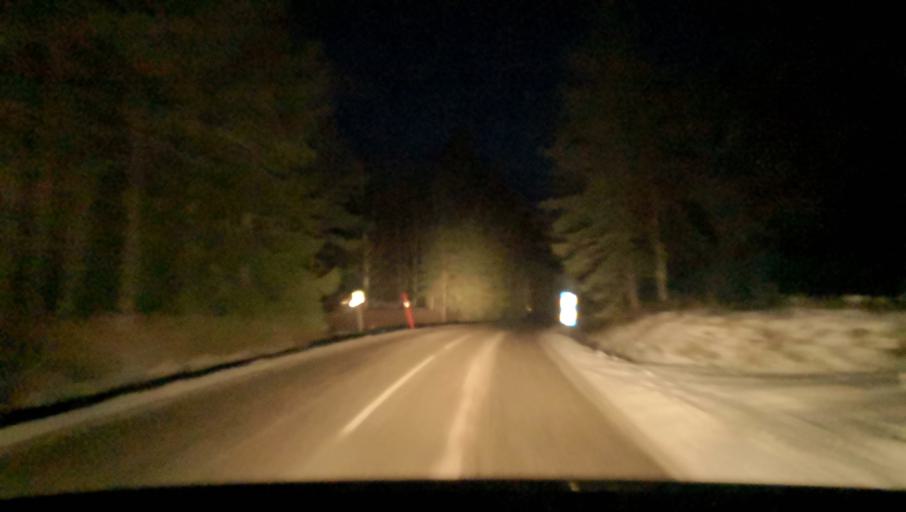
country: SE
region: Soedermanland
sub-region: Flens Kommun
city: Halleforsnas
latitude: 59.1973
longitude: 16.4792
